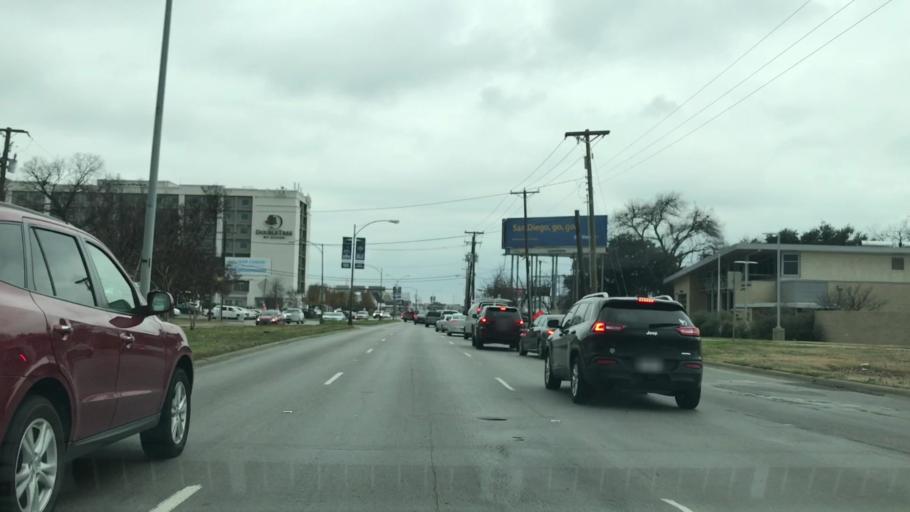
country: US
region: Texas
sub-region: Dallas County
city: University Park
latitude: 32.8360
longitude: -96.8350
